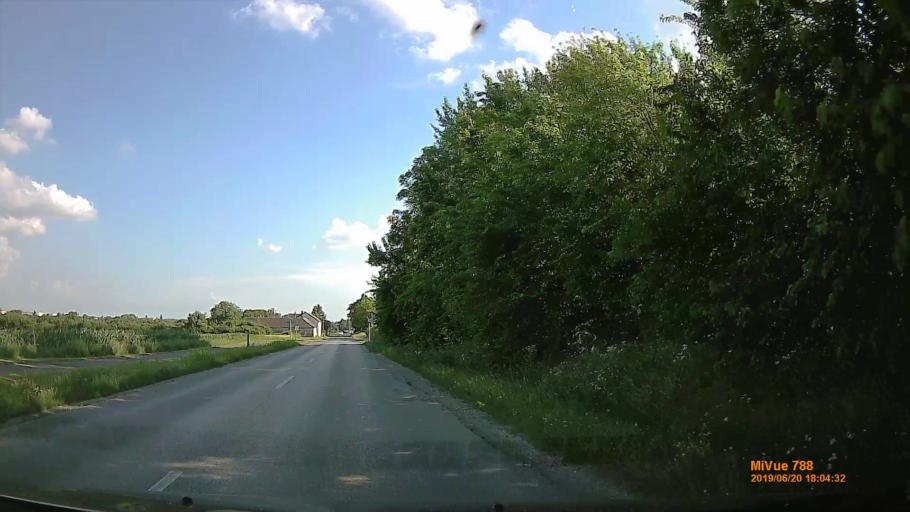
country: HU
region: Baranya
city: Szentlorinc
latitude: 46.0495
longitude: 17.9877
